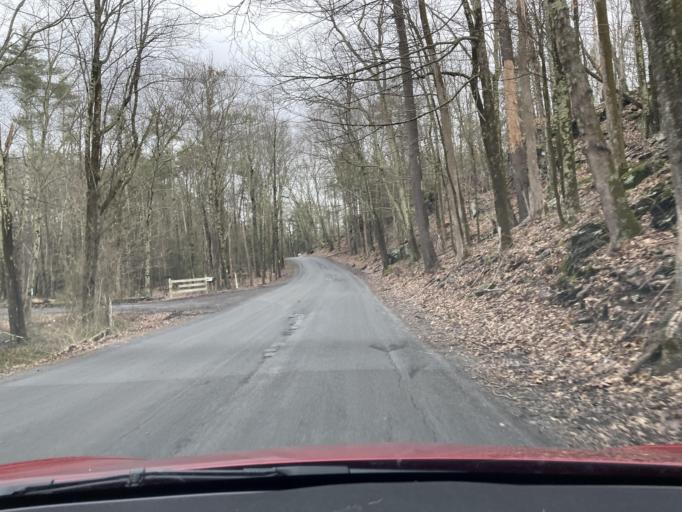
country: US
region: New York
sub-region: Ulster County
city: Manorville
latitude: 42.0996
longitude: -74.0350
